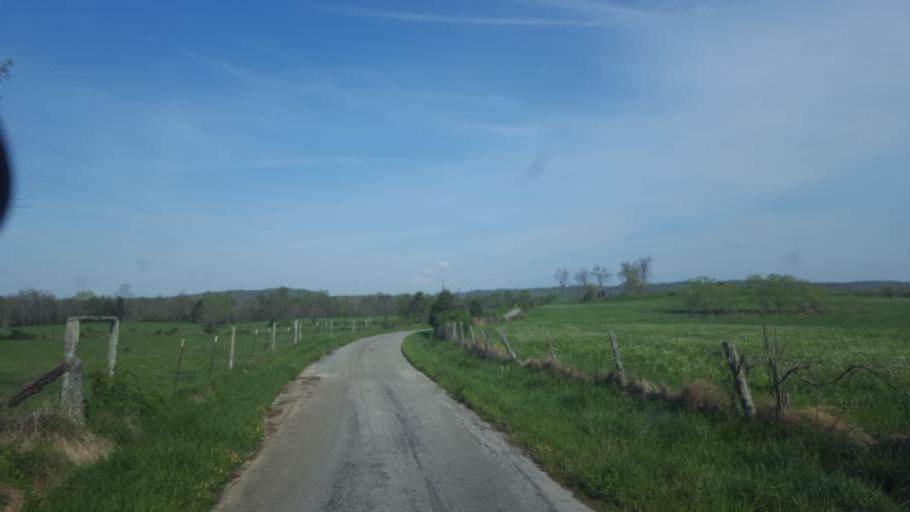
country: US
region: Kentucky
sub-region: Edmonson County
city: Brownsville
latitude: 37.3296
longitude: -86.1094
